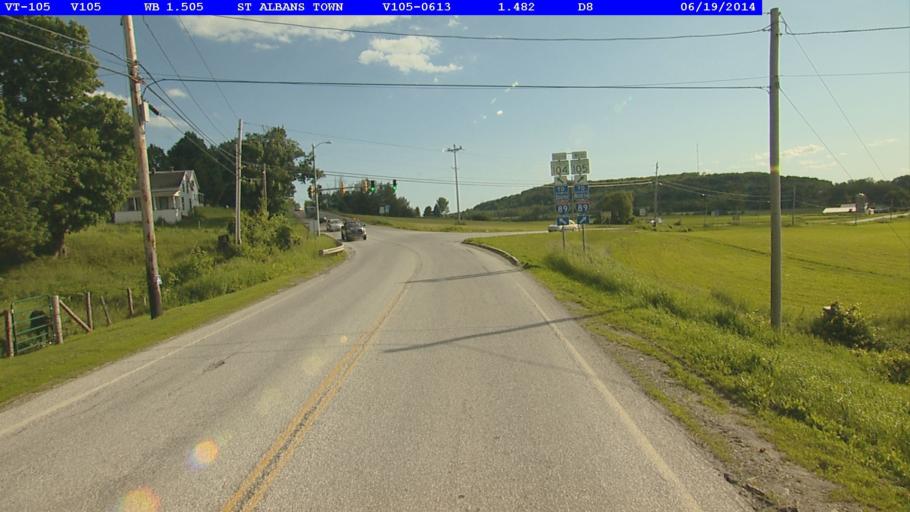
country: US
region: Vermont
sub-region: Franklin County
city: Saint Albans
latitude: 44.8293
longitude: -73.0539
